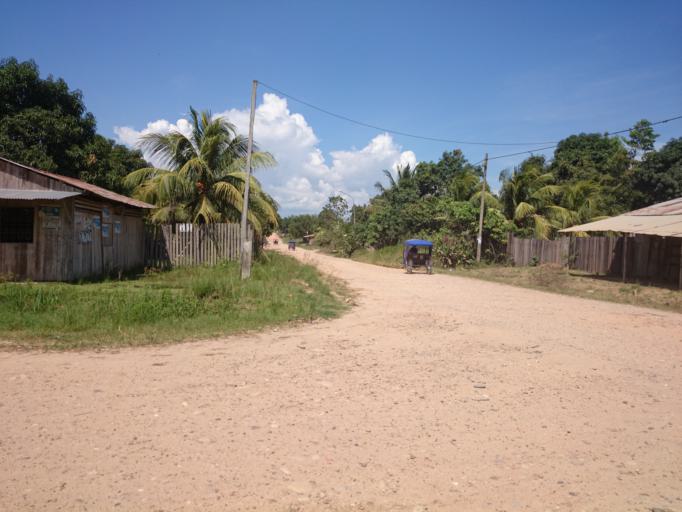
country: PE
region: Ucayali
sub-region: Provincia de Coronel Portillo
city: Puerto Callao
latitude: -8.3596
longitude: -74.5943
